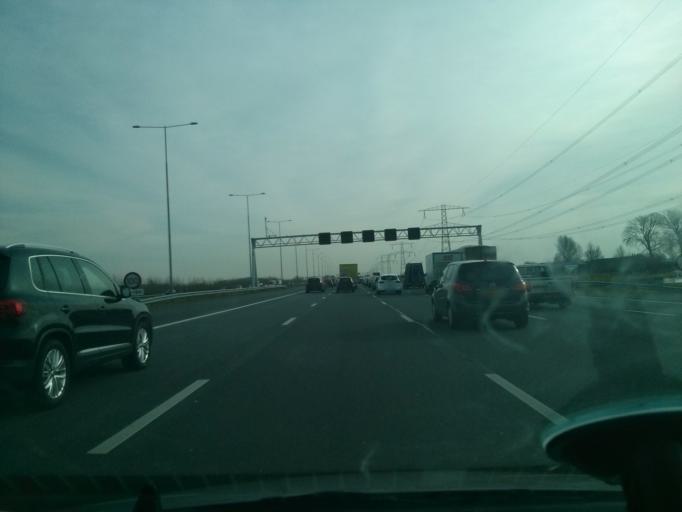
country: NL
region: Utrecht
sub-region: Stichtse Vecht
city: Breukelen
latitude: 52.2022
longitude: 4.9864
